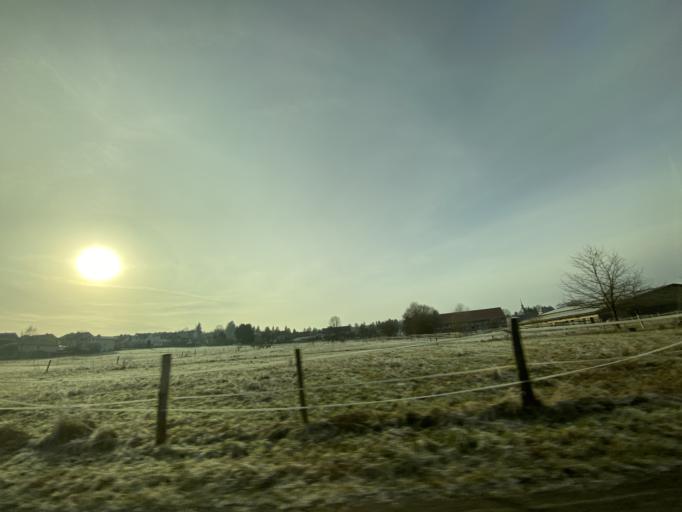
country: DE
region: Hesse
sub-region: Regierungsbezirk Giessen
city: Ebsdorfergrund
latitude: 50.7612
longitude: 8.8860
